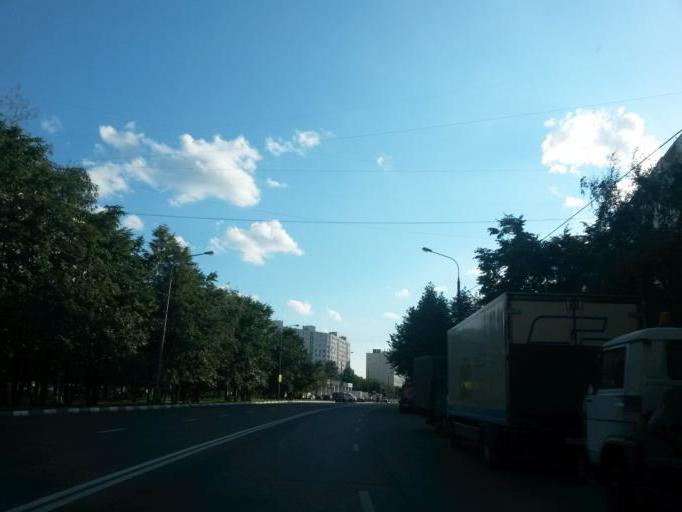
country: RU
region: Moskovskaya
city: Razvilka
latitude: 55.6056
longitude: 37.7415
